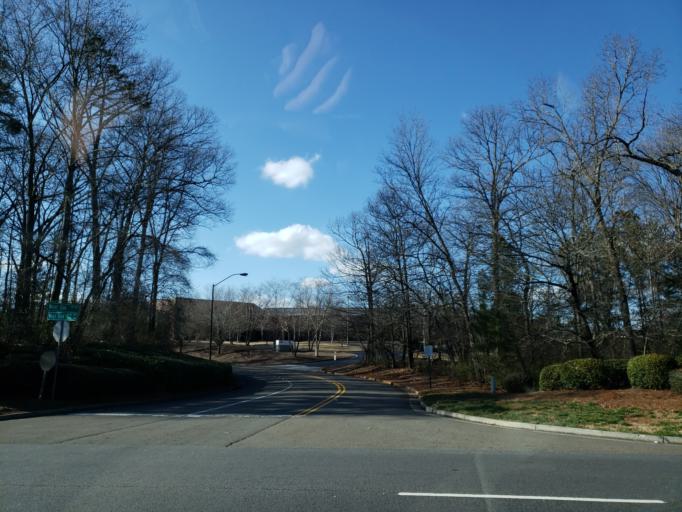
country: US
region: Georgia
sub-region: Cobb County
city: Marietta
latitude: 33.9922
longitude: -84.5242
